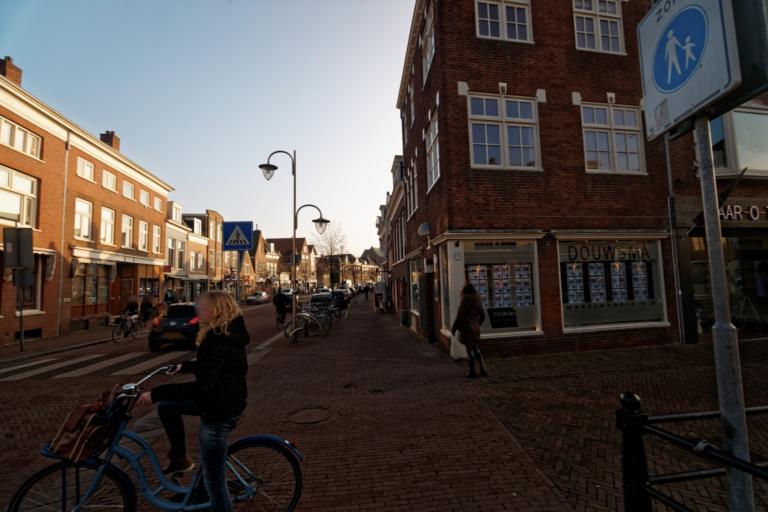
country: NL
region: Friesland
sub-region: Sudwest Fryslan
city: Sneek
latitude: 53.0323
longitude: 5.6623
